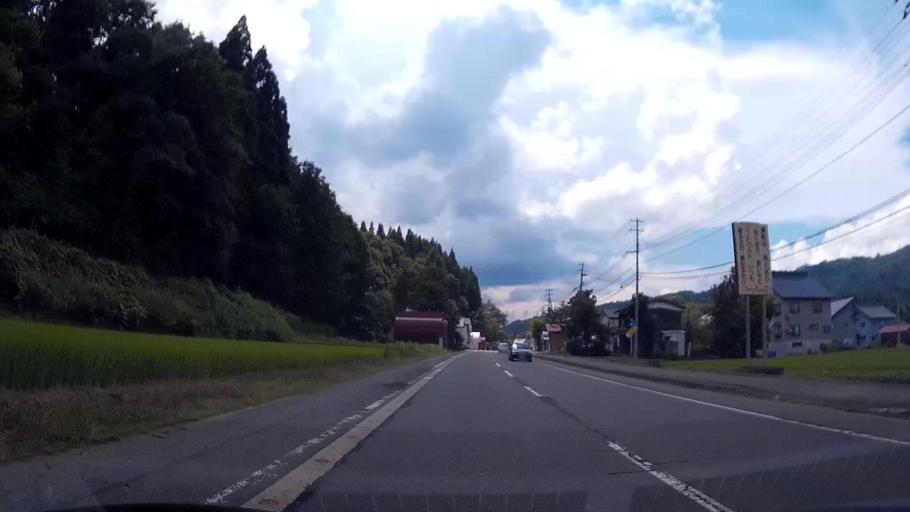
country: JP
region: Niigata
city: Tokamachi
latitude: 36.9950
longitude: 138.5971
